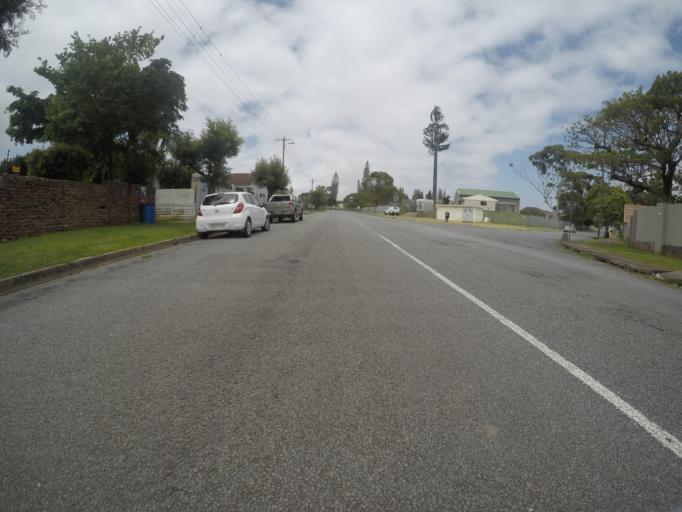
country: ZA
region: Eastern Cape
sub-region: Buffalo City Metropolitan Municipality
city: East London
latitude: -32.9905
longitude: 27.9246
